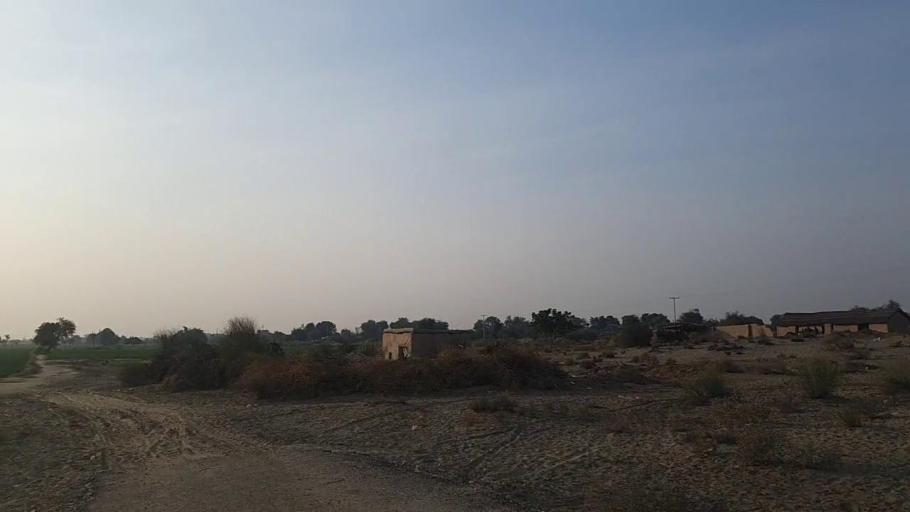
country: PK
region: Sindh
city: Jam Sahib
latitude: 26.4355
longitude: 68.6035
